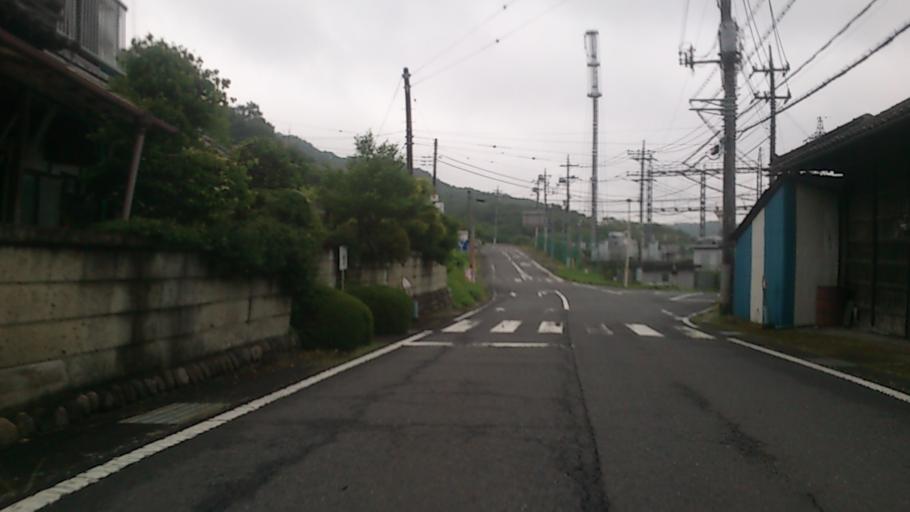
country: JP
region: Ibaraki
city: Omiya
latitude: 36.6220
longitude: 140.3582
